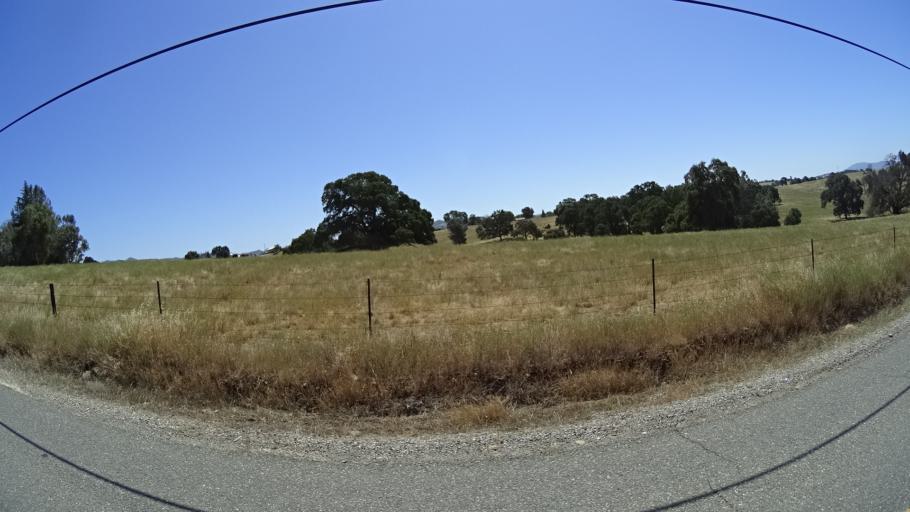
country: US
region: California
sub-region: Calaveras County
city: San Andreas
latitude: 38.1902
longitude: -120.6820
